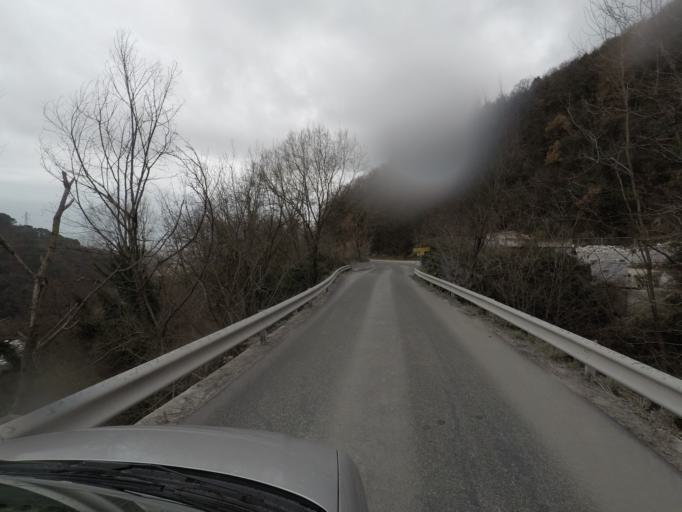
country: IT
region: Tuscany
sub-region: Provincia di Massa-Carrara
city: Carrara
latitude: 44.0849
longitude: 10.1146
